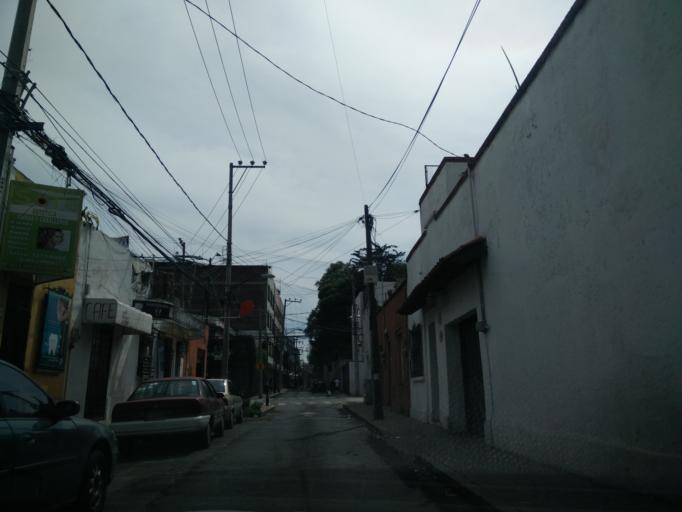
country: MX
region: Mexico City
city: Polanco
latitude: 19.4097
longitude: -99.1859
